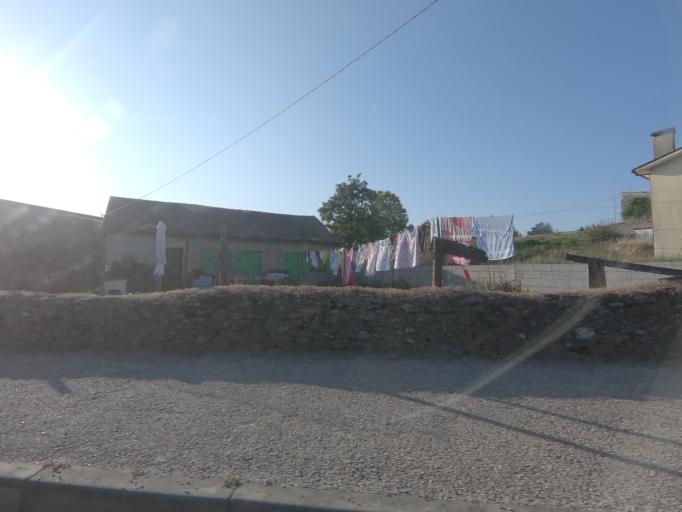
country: PT
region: Vila Real
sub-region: Vila Real
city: Vila Real
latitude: 41.2794
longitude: -7.6903
